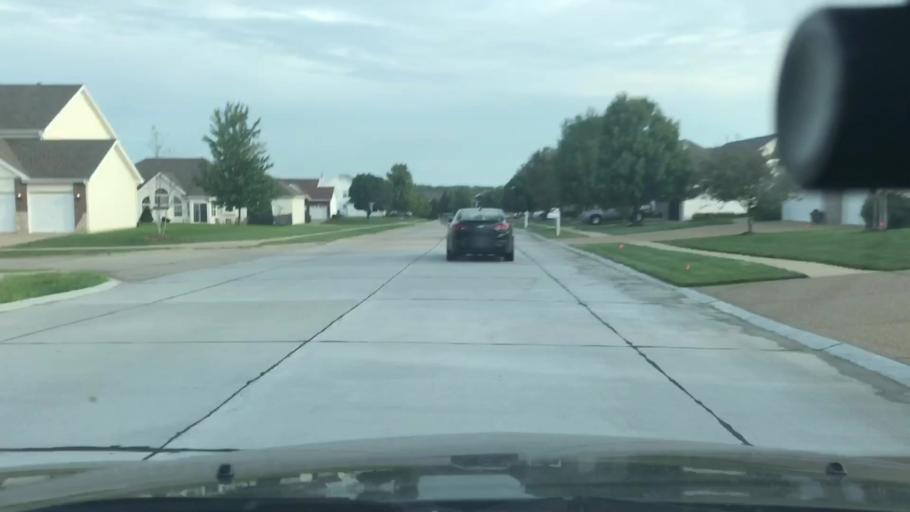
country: US
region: Missouri
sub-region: Saint Charles County
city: Wentzville
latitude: 38.8150
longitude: -90.8899
